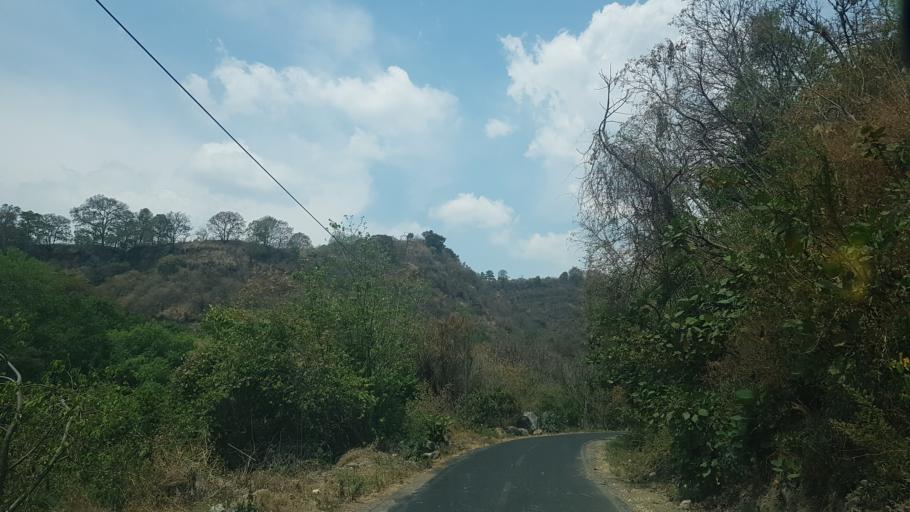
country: MX
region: Puebla
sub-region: Tochimilco
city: La Magdalena Yancuitlalpan
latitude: 18.8719
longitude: -98.6082
